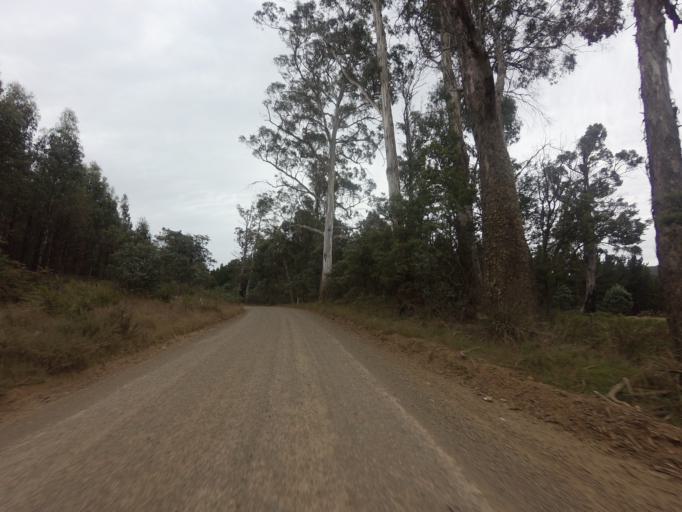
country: AU
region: Tasmania
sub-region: Derwent Valley
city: New Norfolk
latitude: -42.5763
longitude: 147.0012
